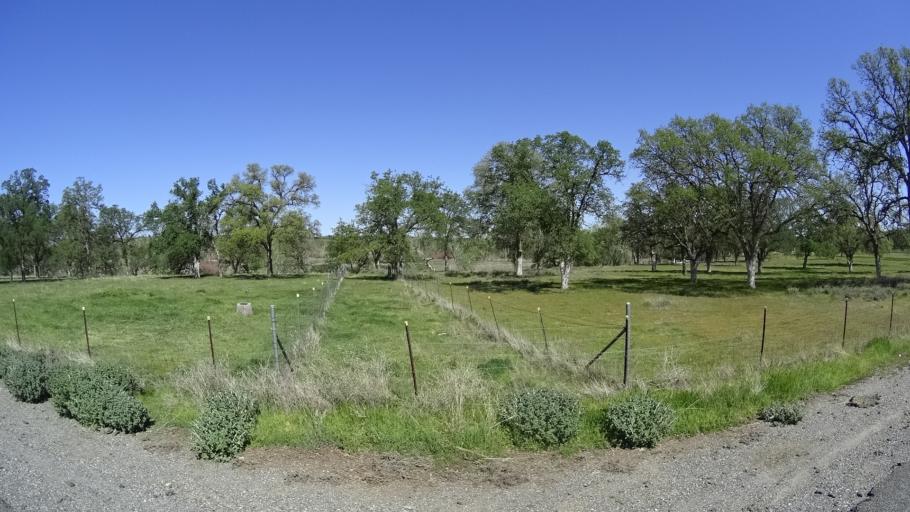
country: US
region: California
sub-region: Glenn County
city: Orland
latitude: 39.7314
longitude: -122.4079
